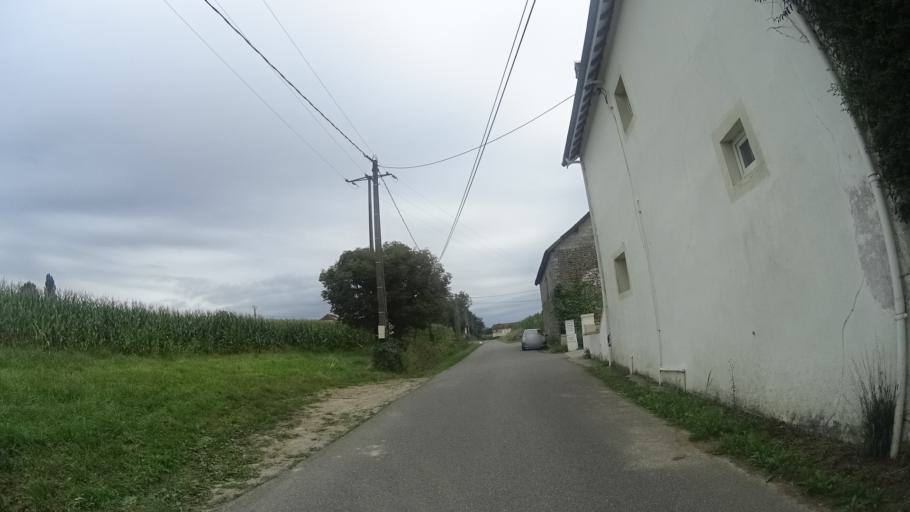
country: FR
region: Aquitaine
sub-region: Departement des Pyrenees-Atlantiques
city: Orthez
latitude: 43.4844
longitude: -0.7207
